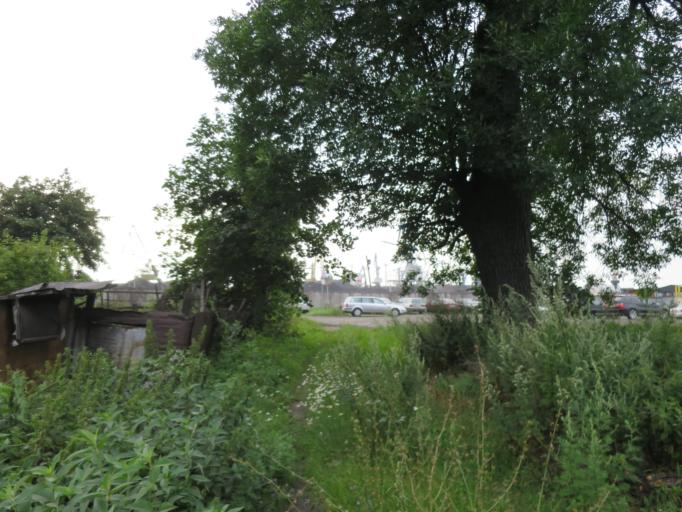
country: LV
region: Riga
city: Riga
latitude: 56.9801
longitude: 24.1001
